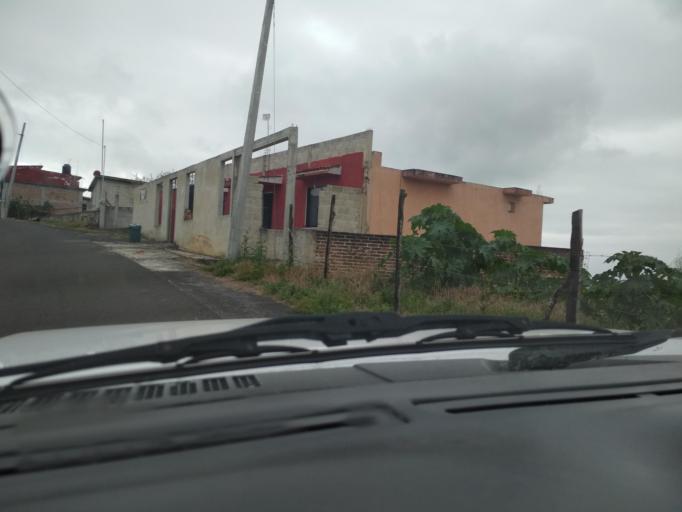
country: MX
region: Veracruz
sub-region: Emiliano Zapata
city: Dos Rios
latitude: 19.5259
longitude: -96.8013
